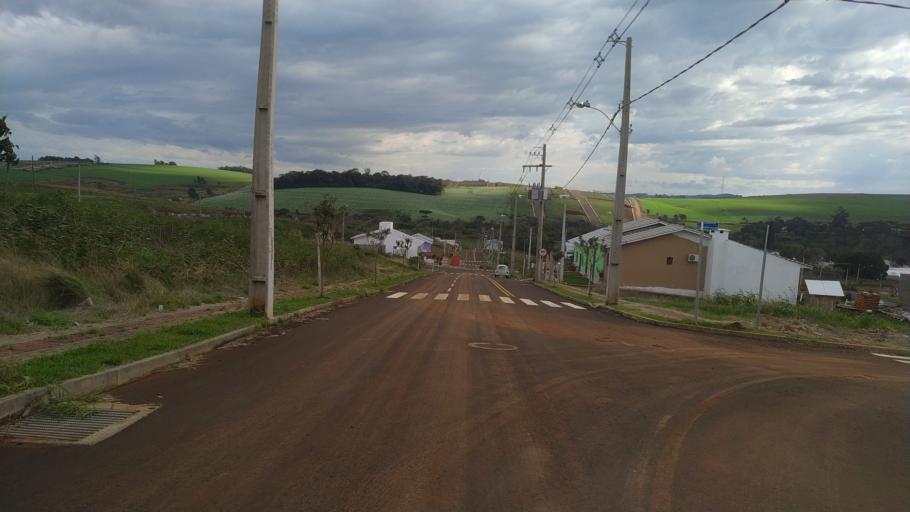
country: BR
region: Santa Catarina
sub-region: Chapeco
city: Chapeco
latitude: -27.0853
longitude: -52.6950
